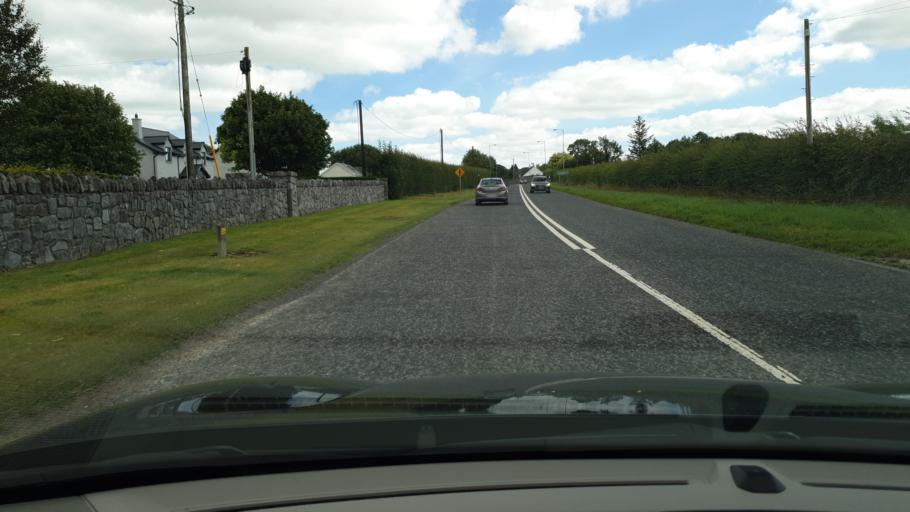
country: IE
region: Leinster
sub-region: An Mhi
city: Newtown Trim
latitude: 53.5283
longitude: -6.6795
